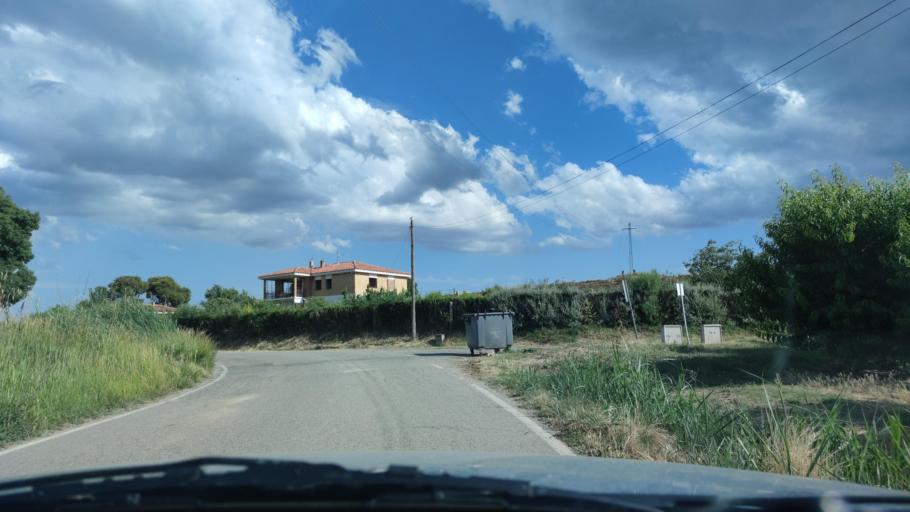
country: ES
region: Catalonia
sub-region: Provincia de Lleida
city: Alpicat
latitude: 41.6278
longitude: 0.5732
